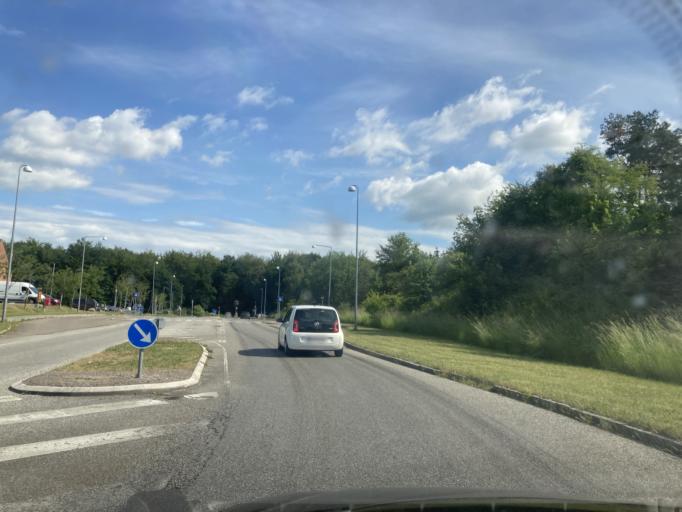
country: DK
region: Capital Region
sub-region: Hillerod Kommune
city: Hillerod
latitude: 55.9302
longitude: 12.3450
